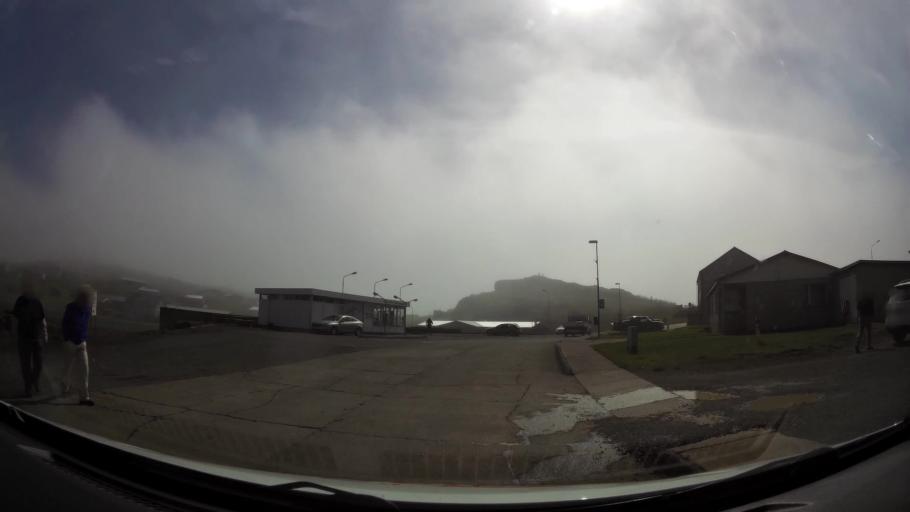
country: IS
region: East
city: Reydarfjoerdur
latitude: 64.6573
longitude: -14.2834
